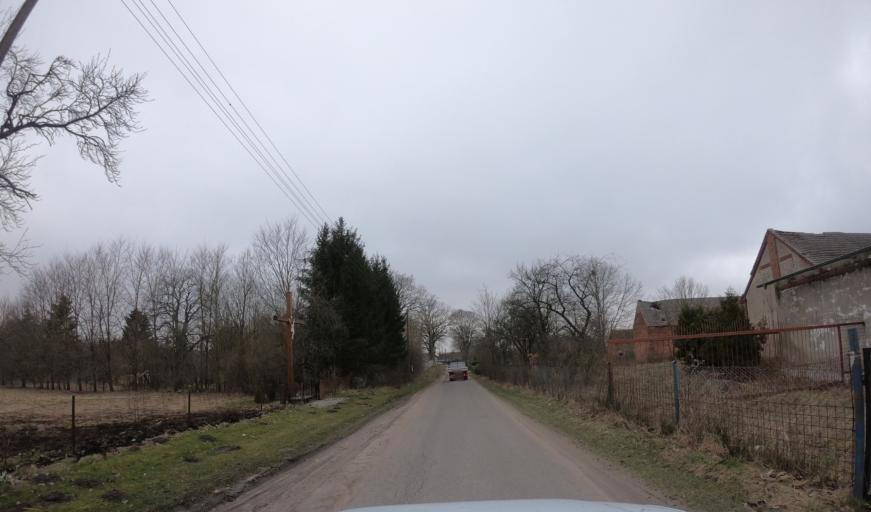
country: PL
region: West Pomeranian Voivodeship
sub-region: Powiat gryficki
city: Ploty
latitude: 53.8463
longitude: 15.2829
